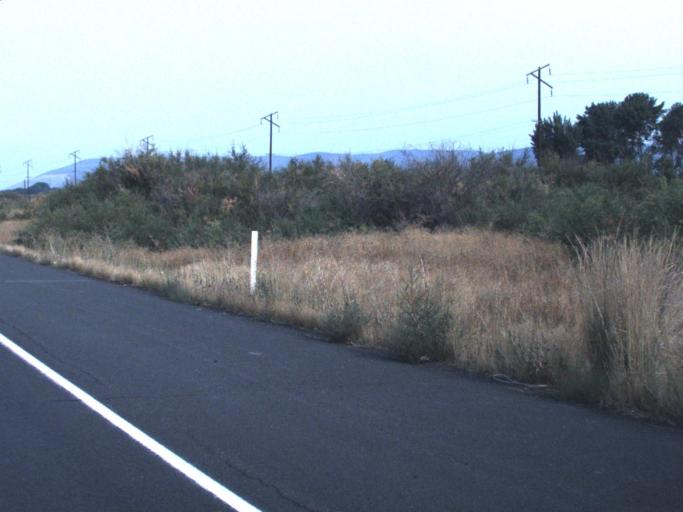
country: US
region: Washington
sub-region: Yakima County
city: Wapato
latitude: 46.4743
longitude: -120.4442
